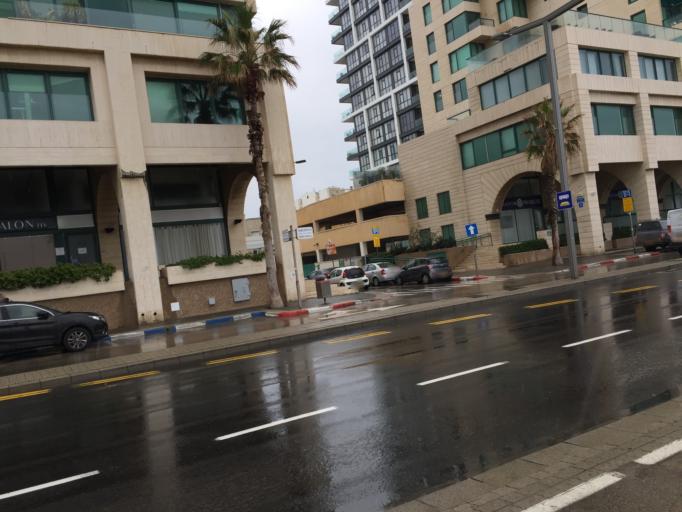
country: IL
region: Tel Aviv
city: Tel Aviv
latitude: 32.0720
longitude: 34.7643
